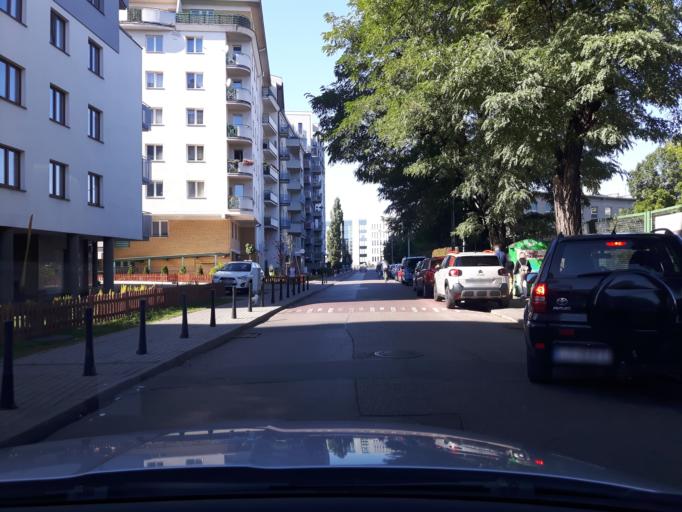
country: PL
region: Masovian Voivodeship
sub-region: Warszawa
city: Praga Poludnie
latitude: 52.2325
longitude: 21.0867
